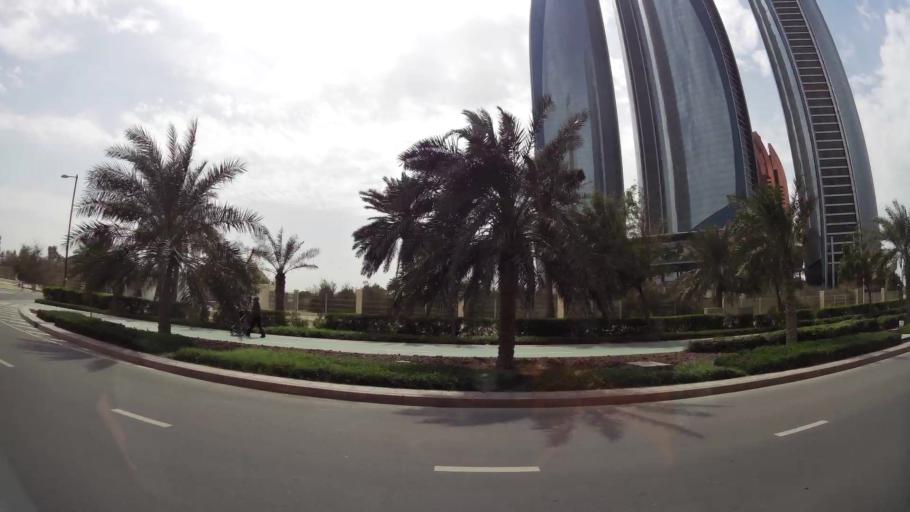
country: AE
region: Abu Dhabi
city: Abu Dhabi
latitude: 24.4603
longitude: 54.3236
